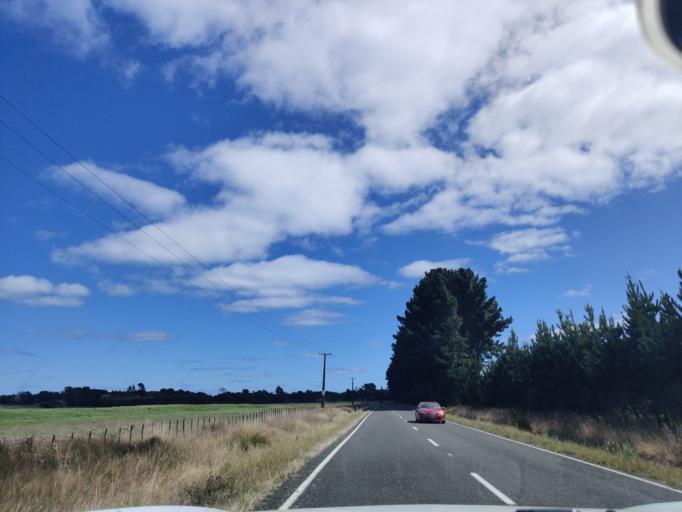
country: NZ
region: Manawatu-Wanganui
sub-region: Horowhenua District
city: Foxton
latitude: -40.3821
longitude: 175.2647
